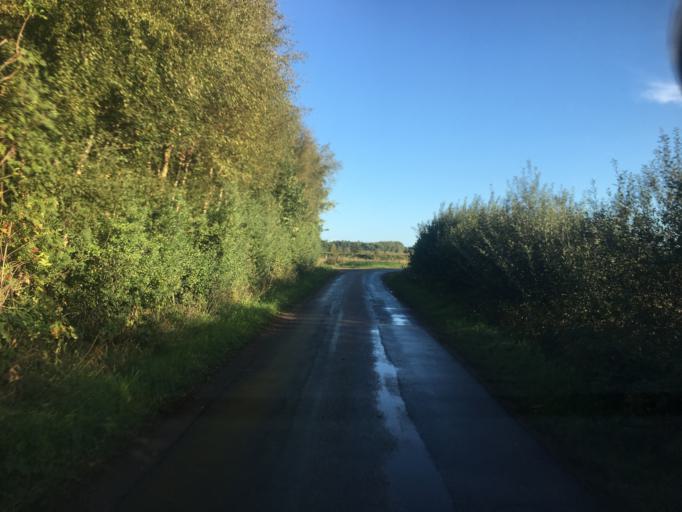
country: DE
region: Schleswig-Holstein
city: Ladelund
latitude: 54.9409
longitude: 9.0207
